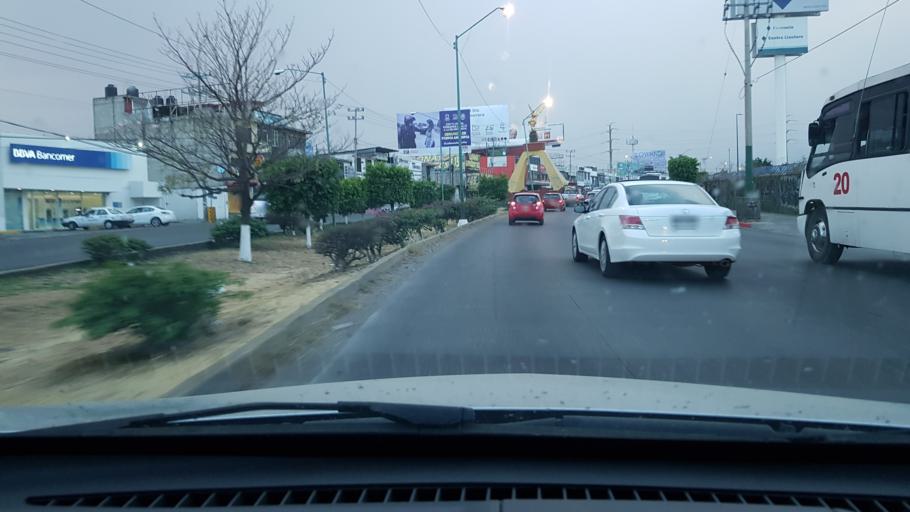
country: MX
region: Morelos
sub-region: Tepoztlan
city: Tetecolala
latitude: 18.9079
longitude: -99.1796
